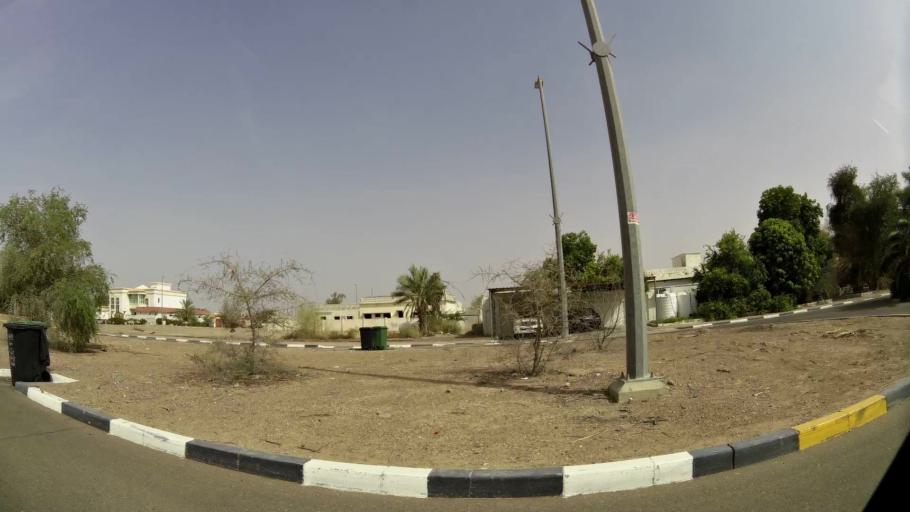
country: AE
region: Abu Dhabi
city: Al Ain
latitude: 24.1847
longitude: 55.6110
